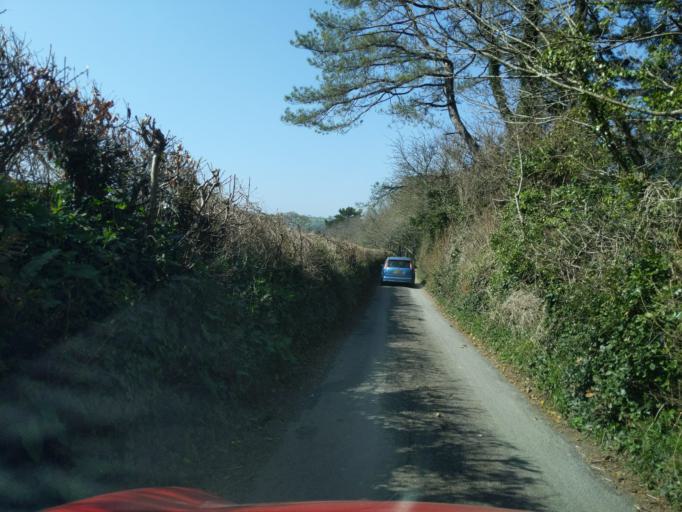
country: GB
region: England
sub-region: Devon
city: Bere Alston
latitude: 50.4543
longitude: -4.1516
